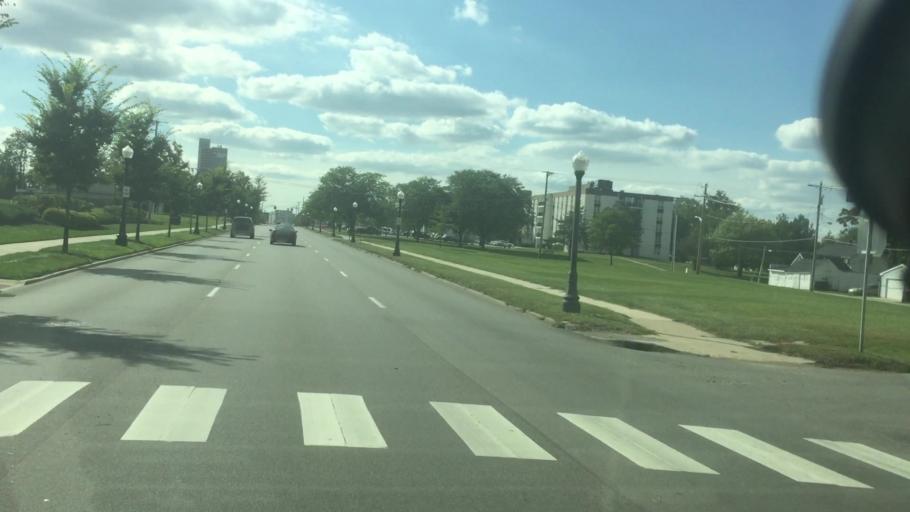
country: US
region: Indiana
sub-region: Allen County
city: Fort Wayne
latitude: 41.0791
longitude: -85.1220
